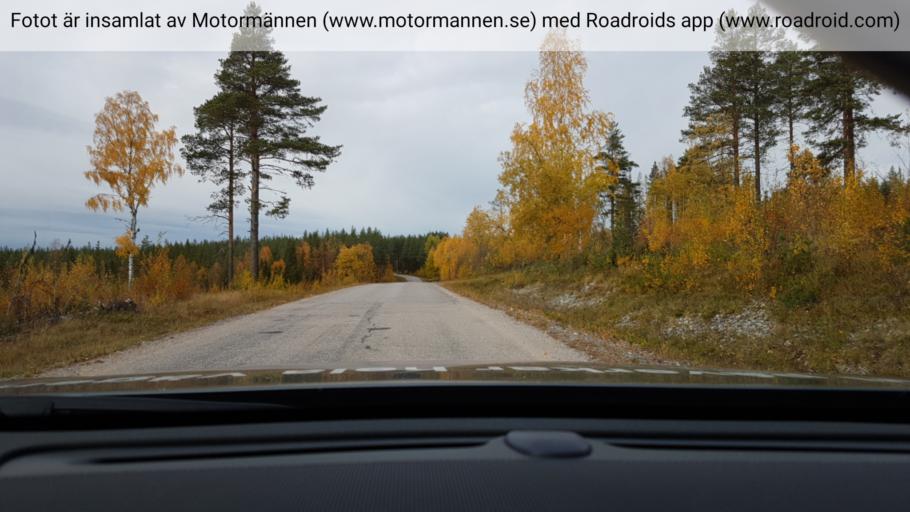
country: SE
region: Norrbotten
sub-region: Overkalix Kommun
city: OEverkalix
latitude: 66.2574
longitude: 23.1135
